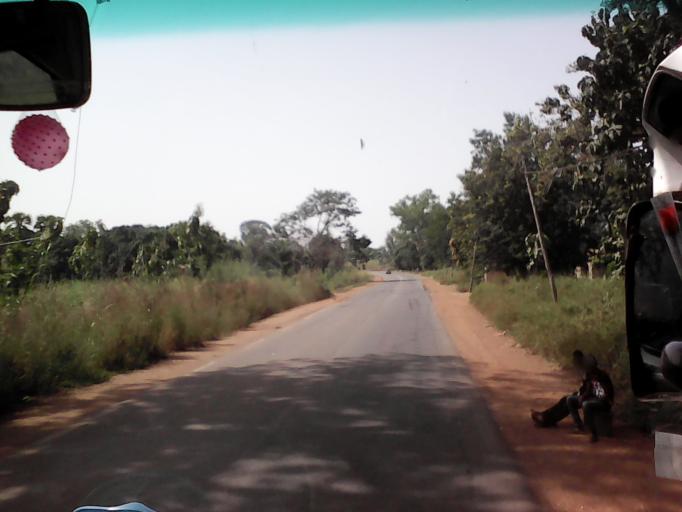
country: TG
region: Centrale
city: Sotouboua
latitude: 8.6977
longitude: 1.0252
